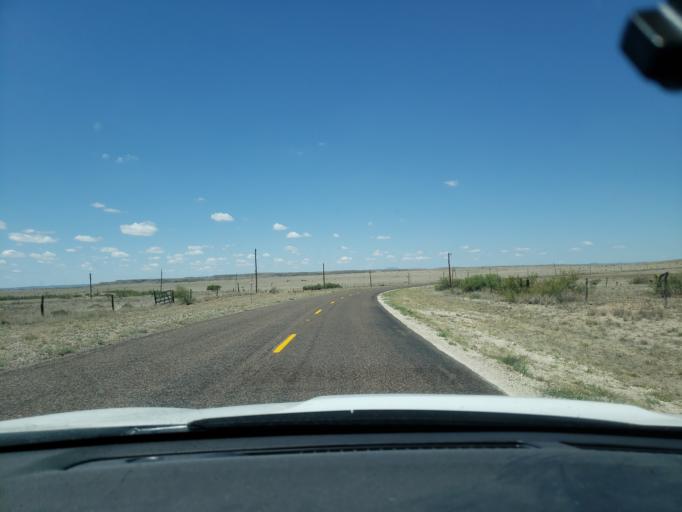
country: US
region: Texas
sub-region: Presidio County
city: Marfa
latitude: 30.2914
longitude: -104.0383
